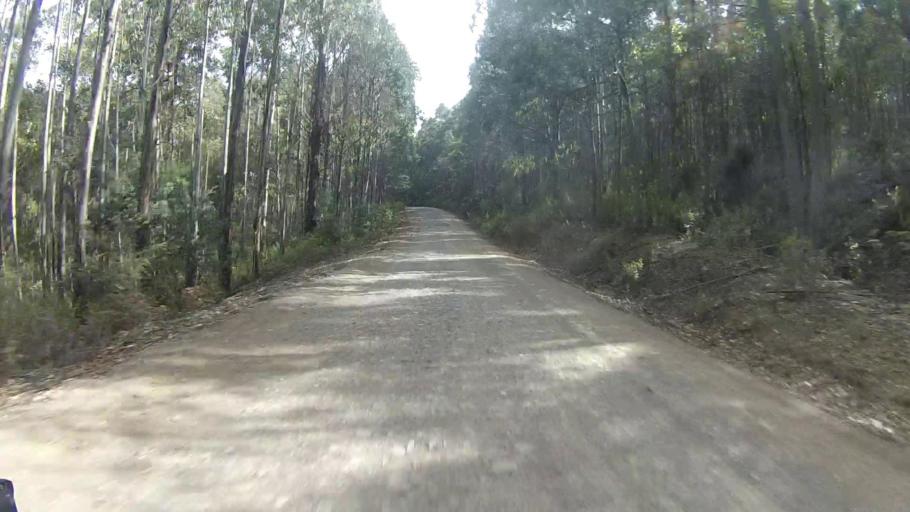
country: AU
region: Tasmania
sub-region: Sorell
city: Sorell
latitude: -42.7482
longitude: 147.8289
